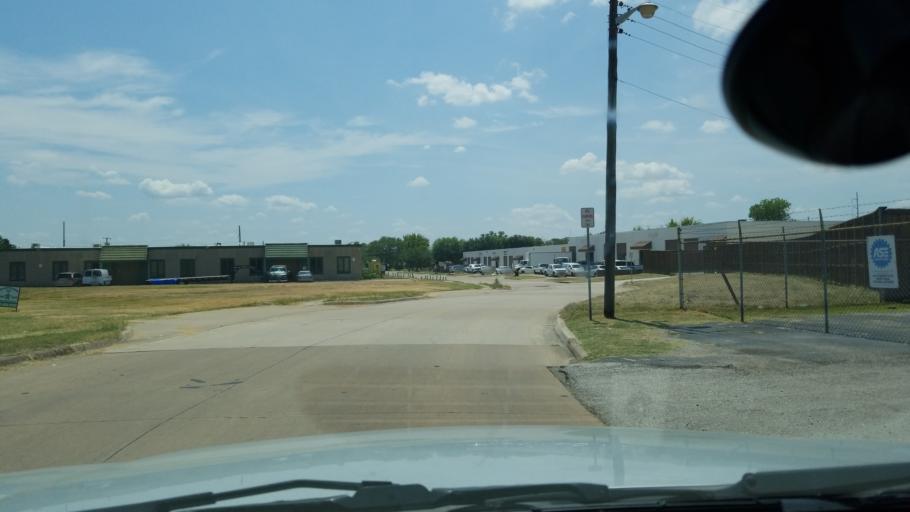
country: US
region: Texas
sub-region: Dallas County
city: Irving
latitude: 32.8239
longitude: -96.9915
